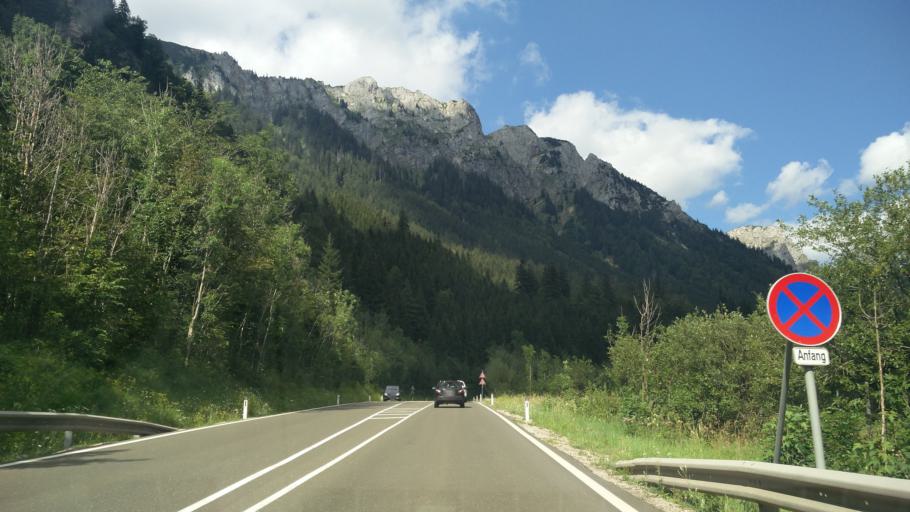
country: AT
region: Styria
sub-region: Politischer Bezirk Leoben
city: Eisenerz
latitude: 47.5491
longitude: 14.9321
